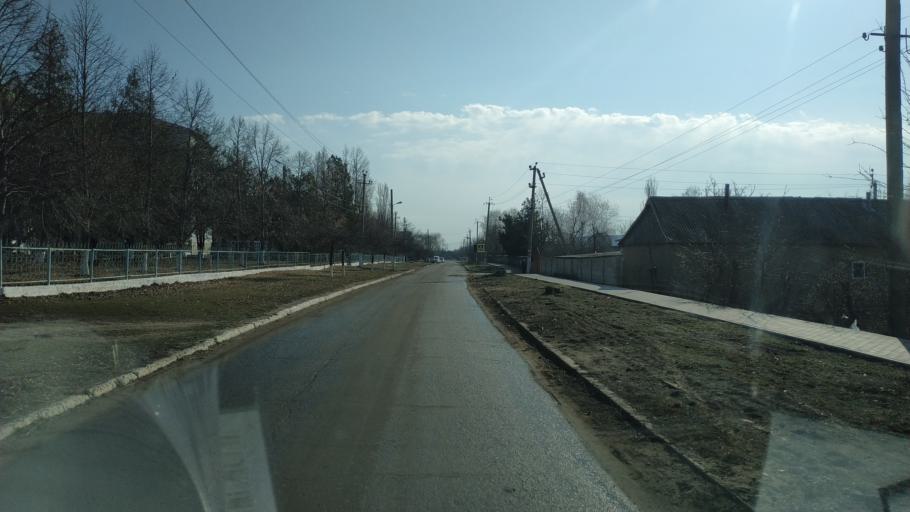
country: MD
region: Chisinau
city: Singera
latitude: 46.6854
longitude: 29.0534
